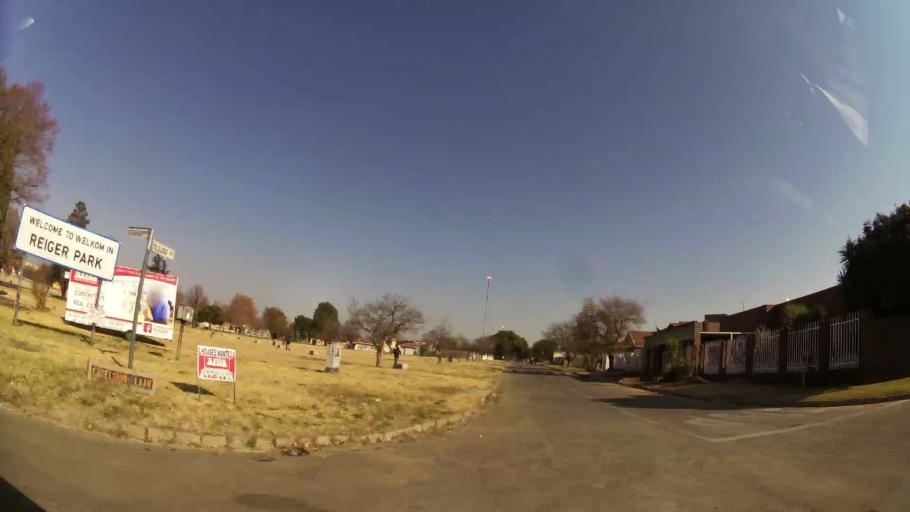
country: ZA
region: Gauteng
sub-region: Ekurhuleni Metropolitan Municipality
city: Boksburg
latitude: -26.2280
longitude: 28.2368
